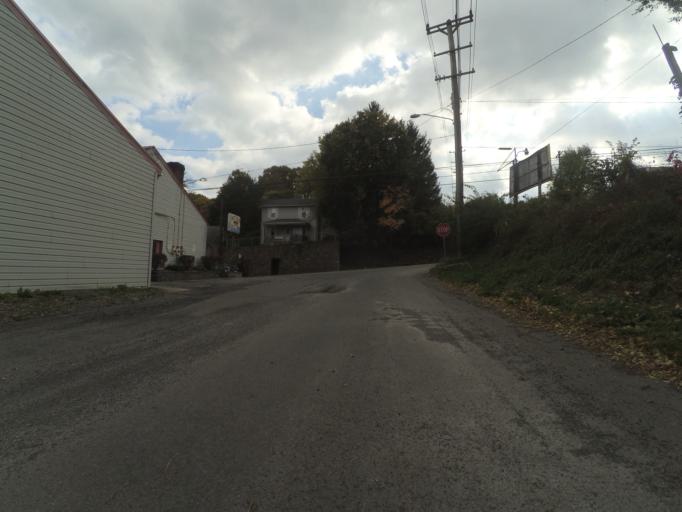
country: US
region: Pennsylvania
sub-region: Centre County
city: Bellefonte
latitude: 40.9044
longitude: -77.7883
